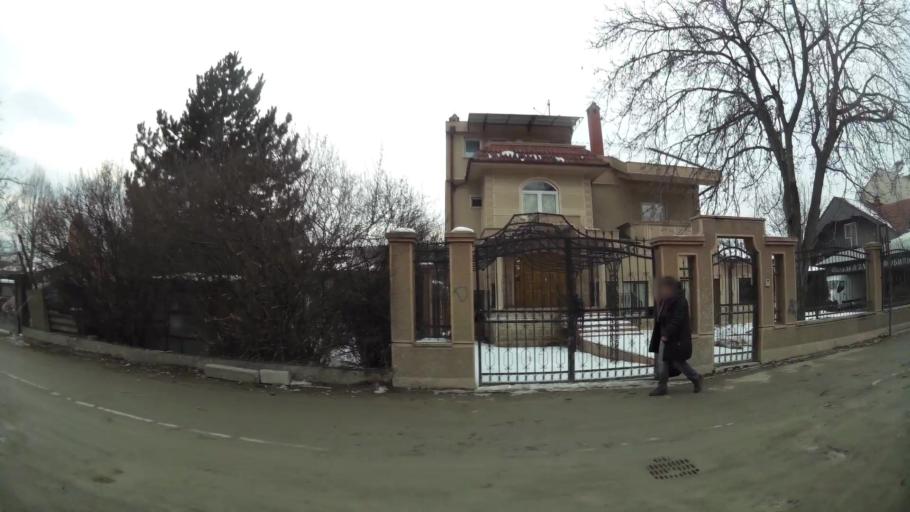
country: MK
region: Butel
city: Butel
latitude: 42.0340
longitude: 21.4457
